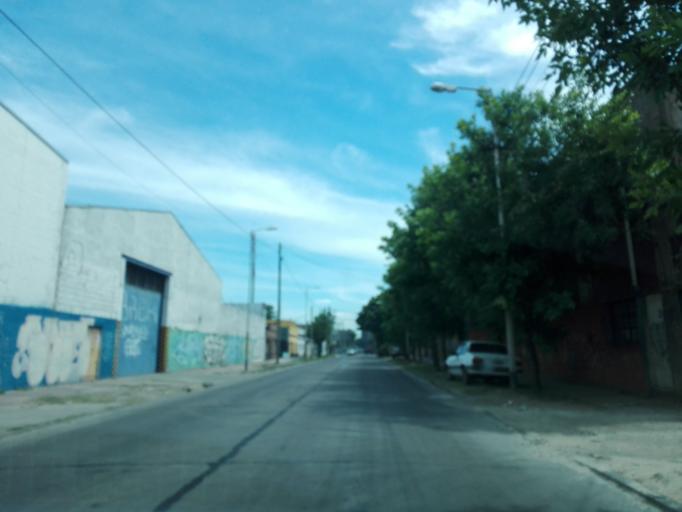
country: AR
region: Buenos Aires
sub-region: Partido de Avellaneda
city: Avellaneda
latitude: -34.6914
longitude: -58.3546
